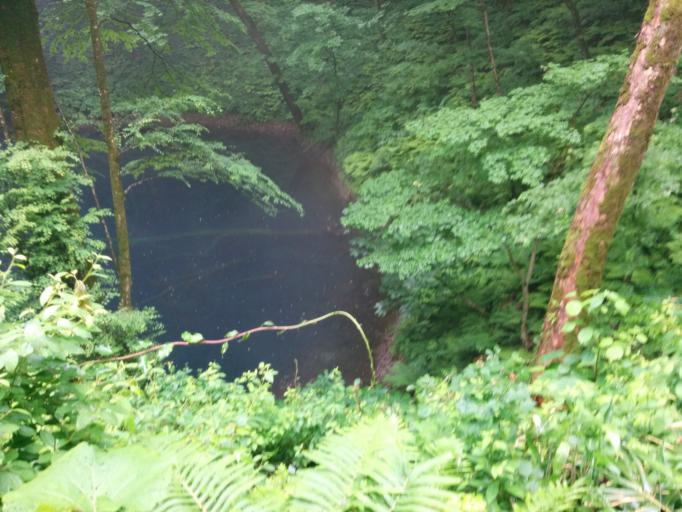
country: JP
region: Akita
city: Noshiromachi
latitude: 40.5604
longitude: 139.9849
